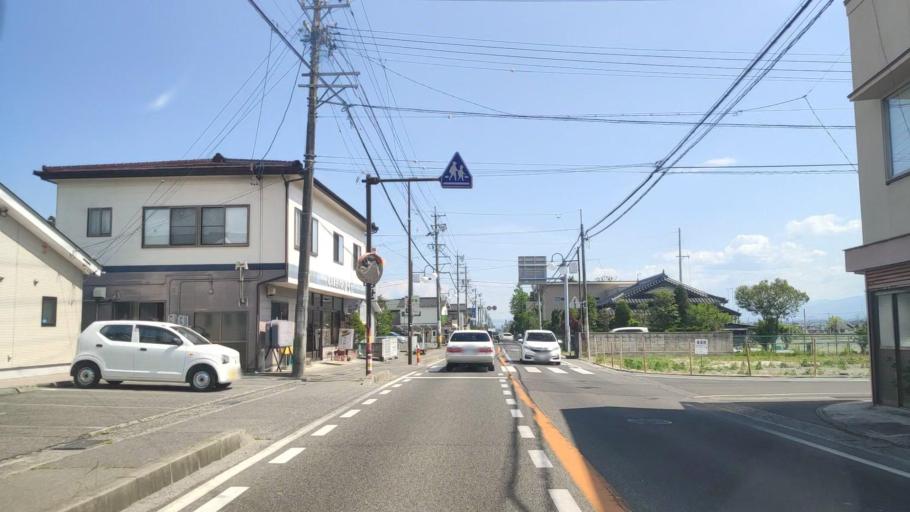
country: JP
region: Nagano
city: Hotaka
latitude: 36.3719
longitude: 137.8742
